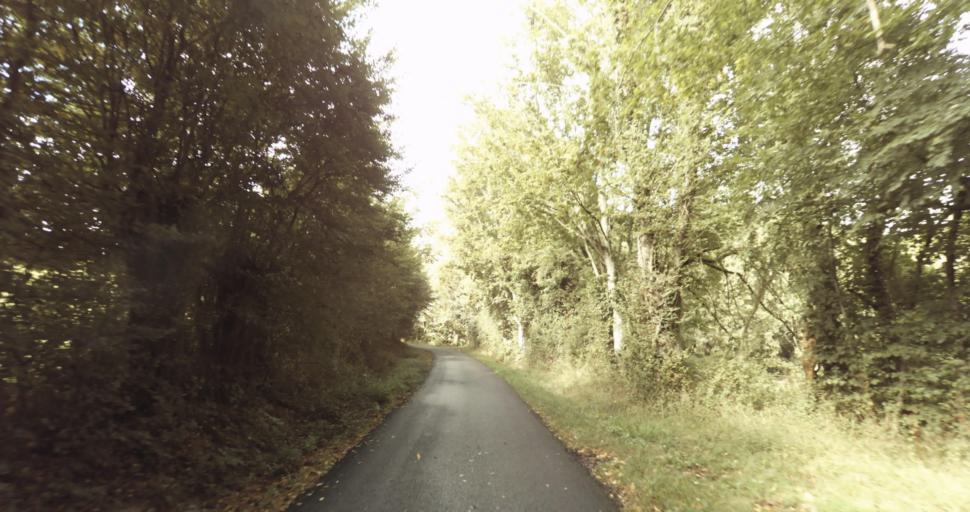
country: FR
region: Lower Normandy
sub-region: Departement de l'Orne
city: Gace
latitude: 48.7998
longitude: 0.2666
